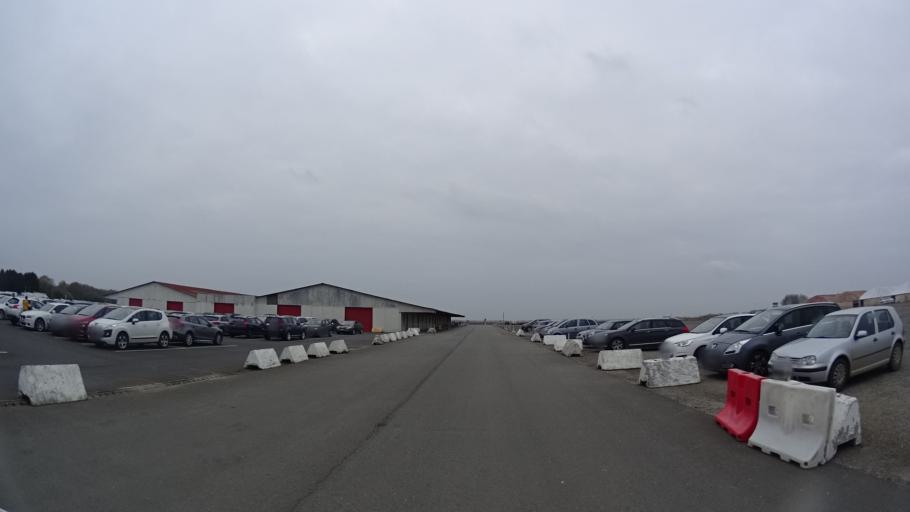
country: FR
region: Brittany
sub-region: Departement d'Ille-et-Vilaine
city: Saint-Jacques-de-la-Lande
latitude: 48.0603
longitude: -1.7299
